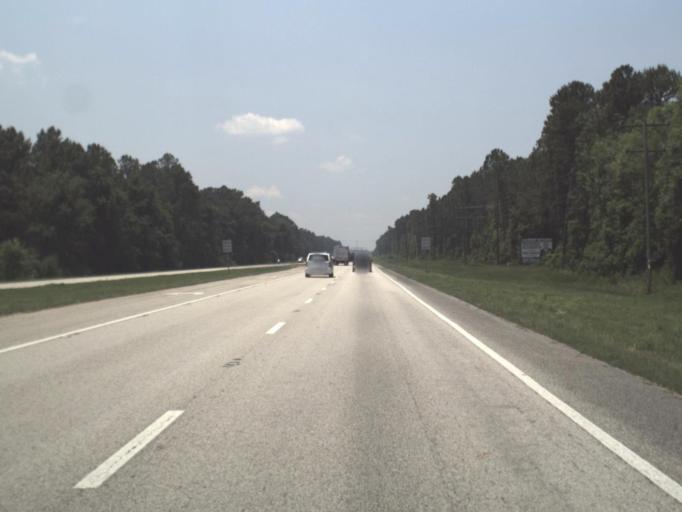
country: US
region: Florida
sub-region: Baker County
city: Macclenny
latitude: 30.1589
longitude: -82.0304
